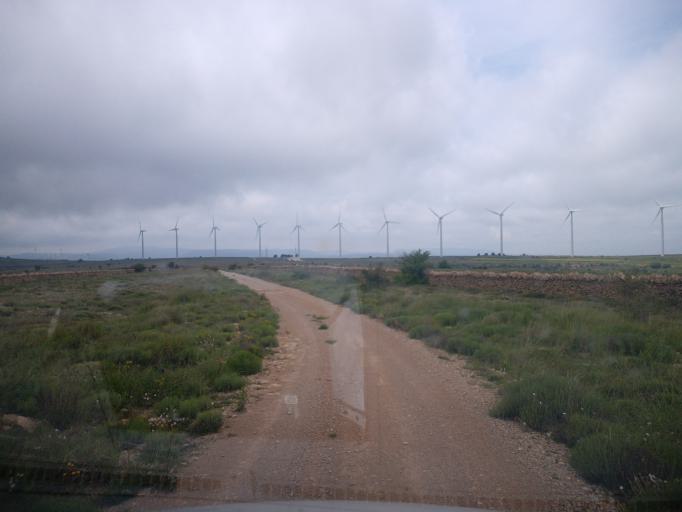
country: ES
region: Valencia
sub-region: Provincia de Castello
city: Castellfort
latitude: 40.4665
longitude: -0.1980
